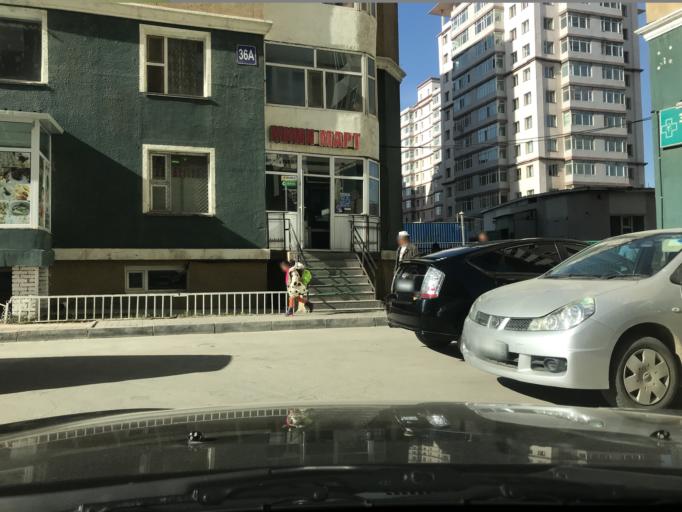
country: MN
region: Ulaanbaatar
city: Ulaanbaatar
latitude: 47.9119
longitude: 106.9474
